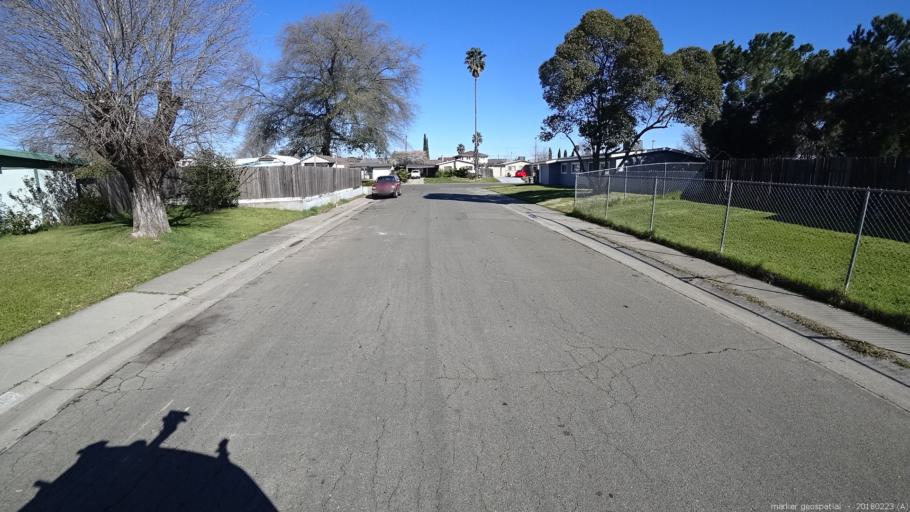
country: US
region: California
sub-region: Sacramento County
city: North Highlands
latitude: 38.7053
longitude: -121.3913
